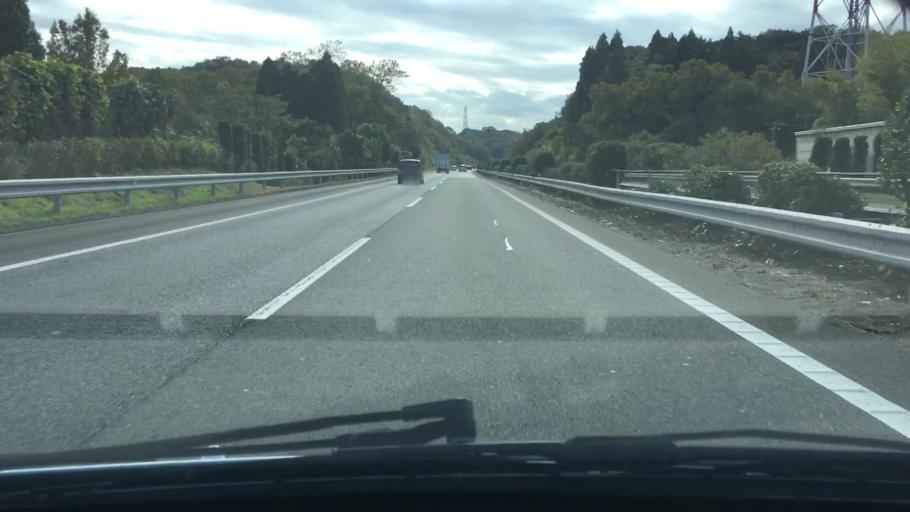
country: JP
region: Chiba
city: Ichihara
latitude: 35.4723
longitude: 140.0832
